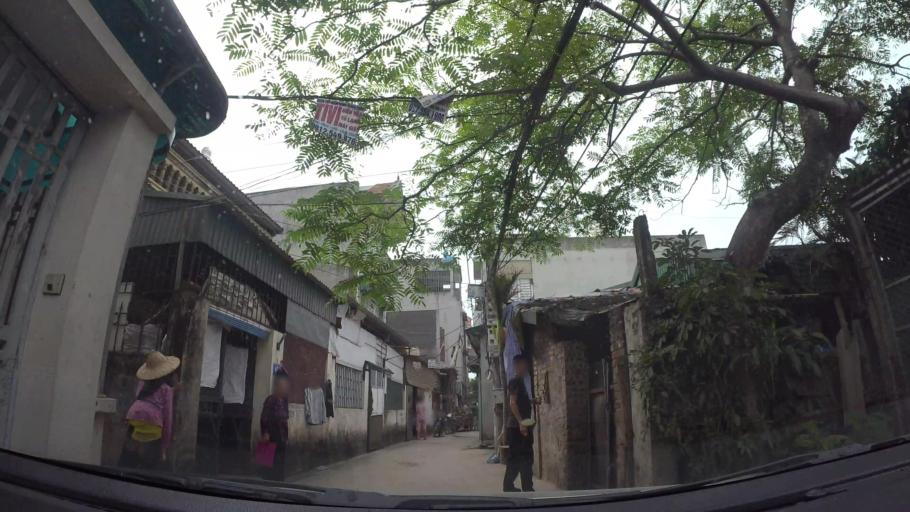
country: VN
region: Ha Noi
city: Tay Ho
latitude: 21.0845
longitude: 105.8179
